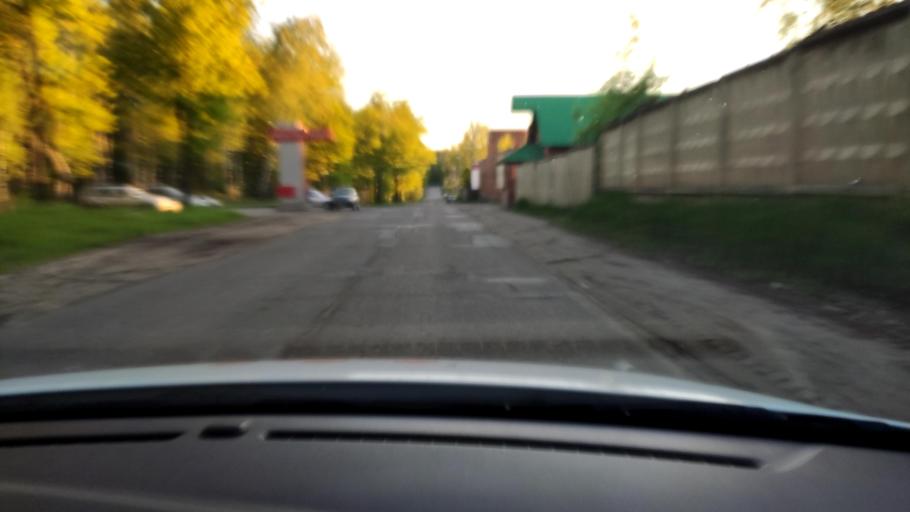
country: RU
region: Tatarstan
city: Vysokaya Gora
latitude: 55.9276
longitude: 49.3104
